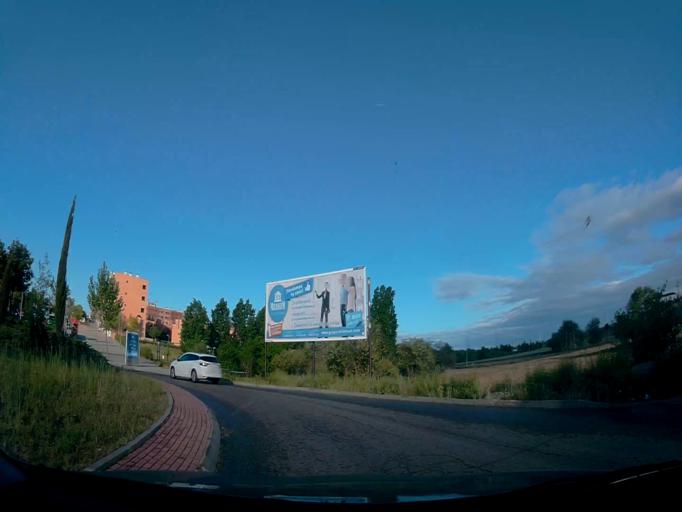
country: ES
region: Madrid
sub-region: Provincia de Madrid
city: San Sebastian de los Reyes
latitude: 40.5635
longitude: -3.6176
